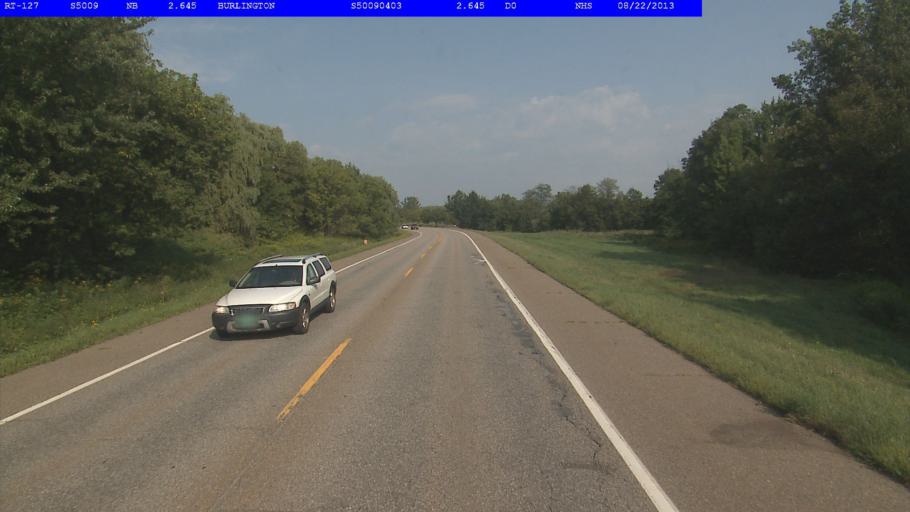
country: US
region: Vermont
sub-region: Chittenden County
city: Burlington
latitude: 44.5196
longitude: -73.2437
